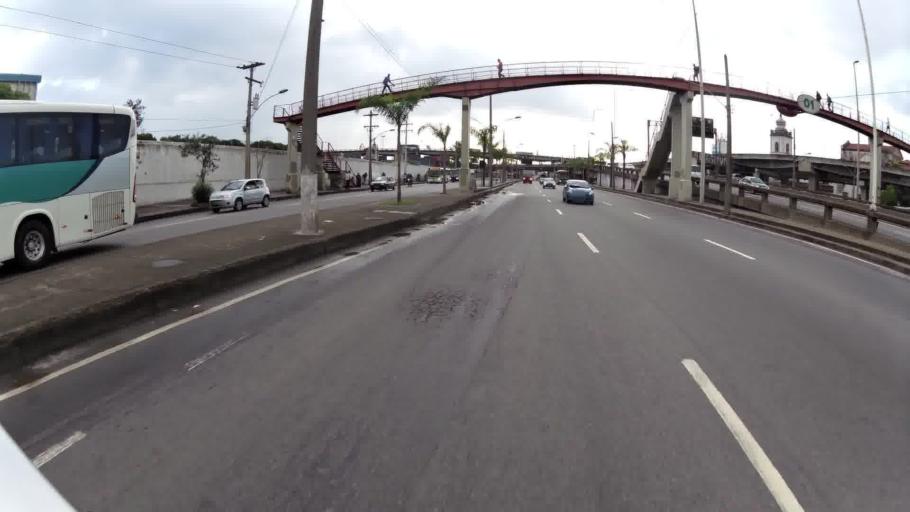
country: BR
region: Rio de Janeiro
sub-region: Rio De Janeiro
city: Rio de Janeiro
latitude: -22.8888
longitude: -43.2210
